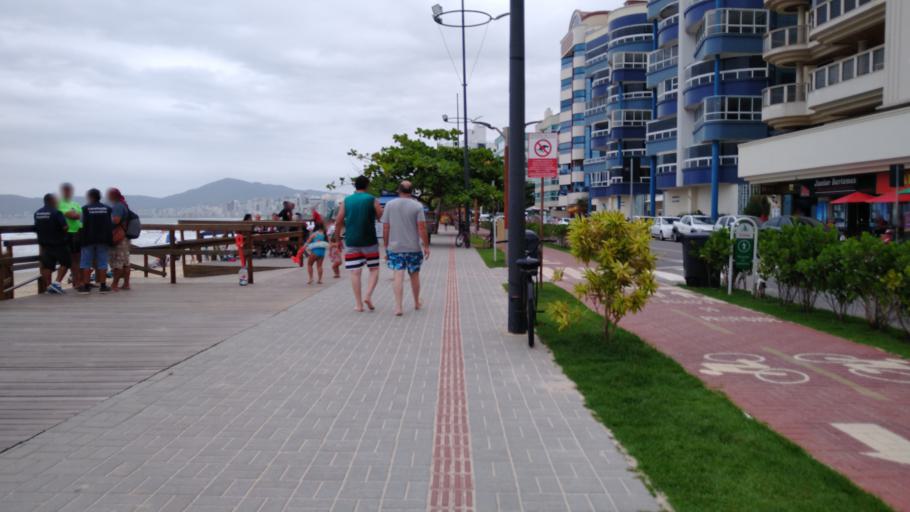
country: BR
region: Santa Catarina
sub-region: Itapema
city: Itapema
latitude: -27.1004
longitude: -48.6140
